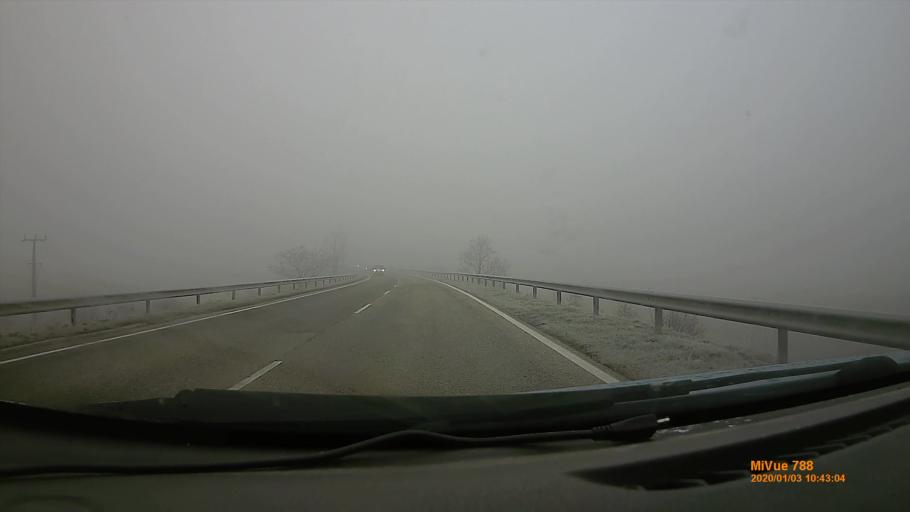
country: HU
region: Tolna
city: Bataszek
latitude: 46.2069
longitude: 18.7082
